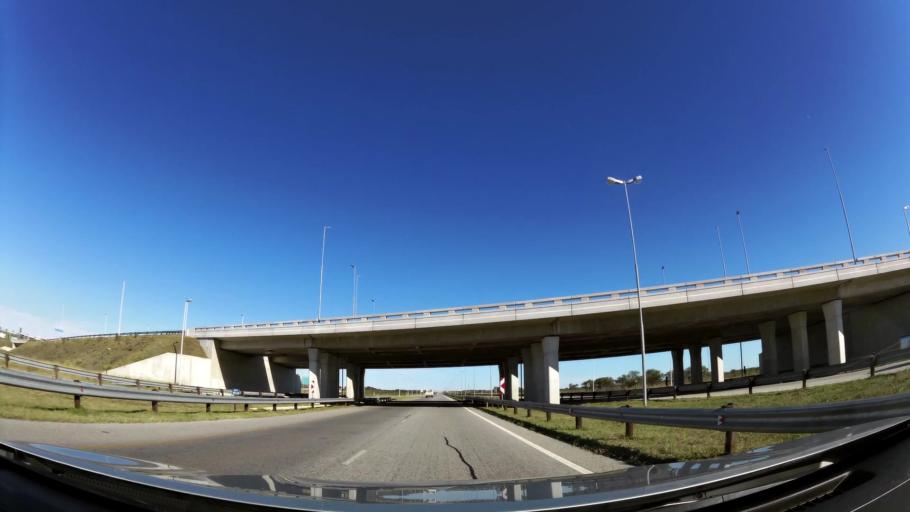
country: ZA
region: Eastern Cape
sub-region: Nelson Mandela Bay Metropolitan Municipality
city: Port Elizabeth
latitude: -33.9471
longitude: 25.4655
